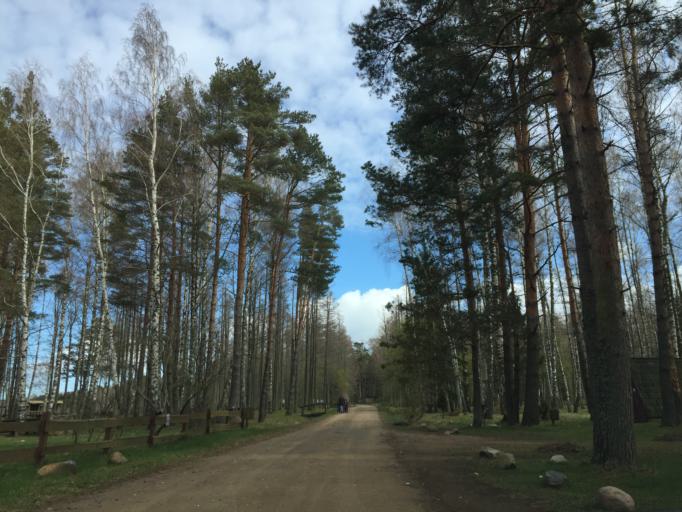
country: LV
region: Salacgrivas
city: Salacgriva
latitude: 57.5808
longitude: 24.3656
